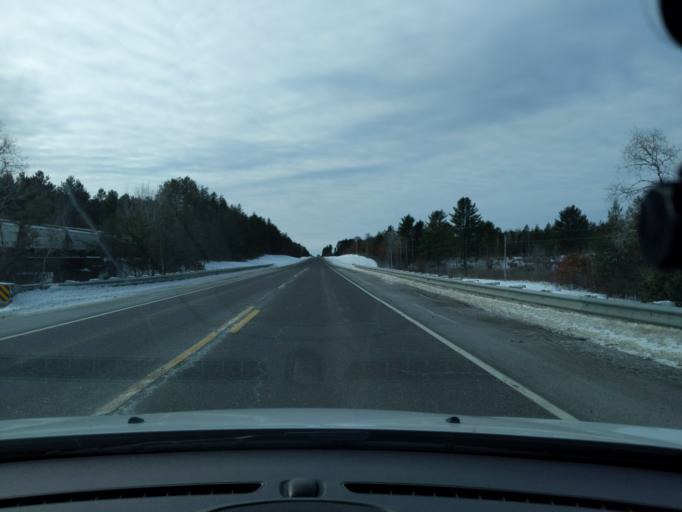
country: US
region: Wisconsin
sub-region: Washburn County
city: Spooner
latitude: 45.9218
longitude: -91.7298
